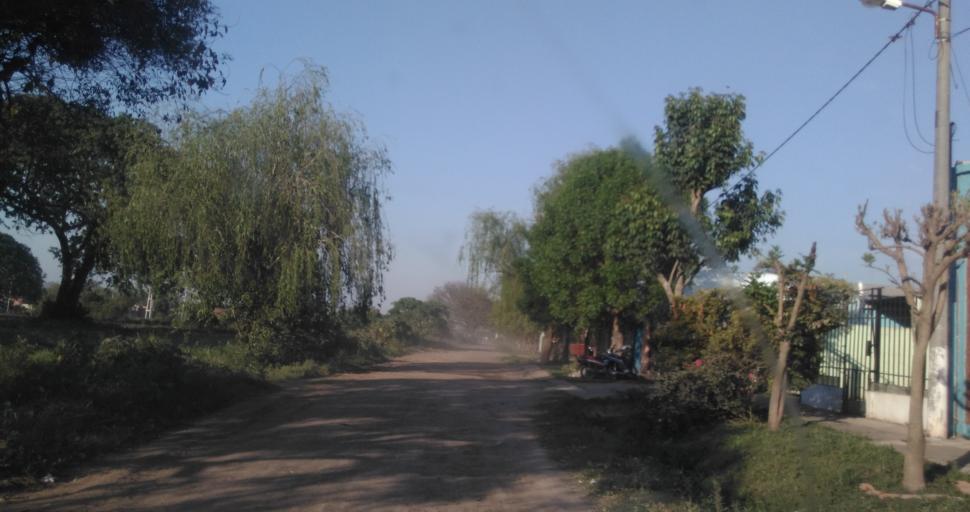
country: AR
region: Chaco
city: Fontana
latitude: -27.4120
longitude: -59.0321
